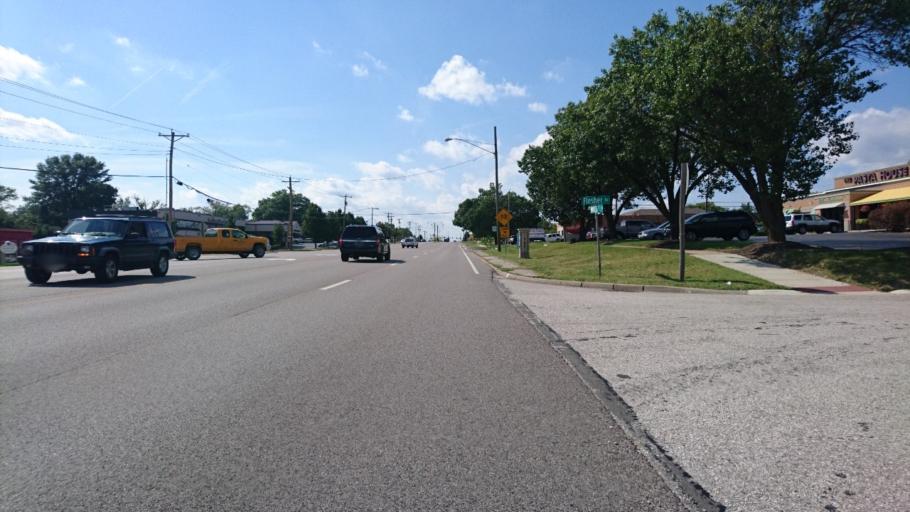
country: US
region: Missouri
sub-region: Saint Louis County
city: Ellisville
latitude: 38.5928
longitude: -90.5717
